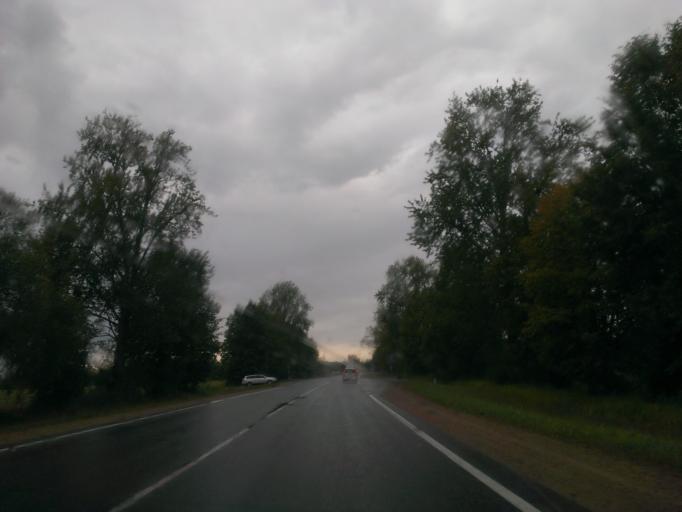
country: LV
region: Kegums
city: Kegums
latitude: 56.7728
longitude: 24.6648
